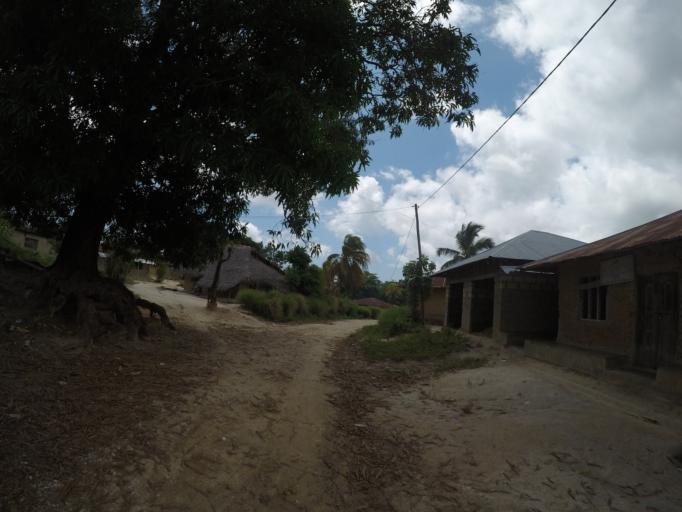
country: TZ
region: Pemba South
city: Mtambile
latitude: -5.3933
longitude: 39.7398
